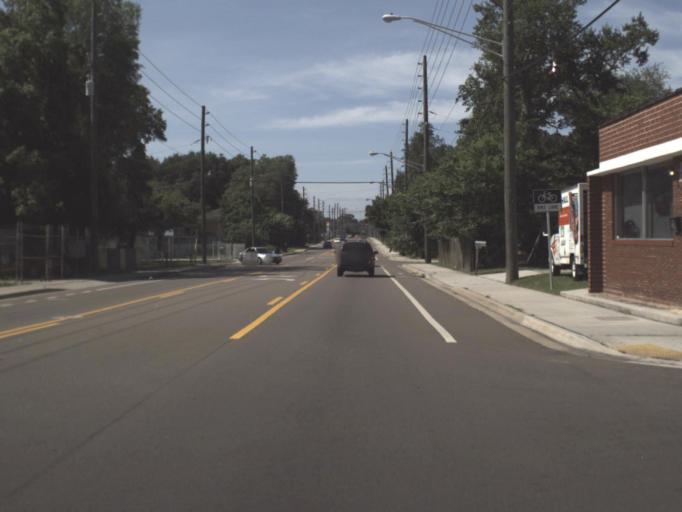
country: US
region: Florida
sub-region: Duval County
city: Jacksonville
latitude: 30.3184
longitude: -81.7055
